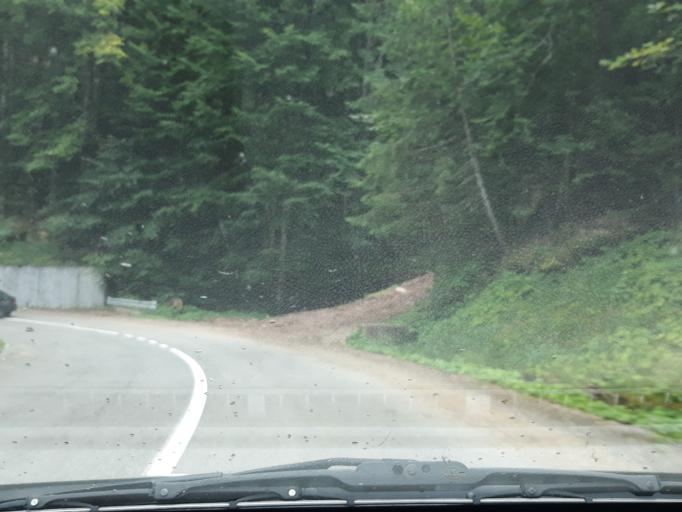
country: RO
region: Bihor
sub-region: Comuna Pietroasa
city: Pietroasa
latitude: 46.5960
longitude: 22.6725
